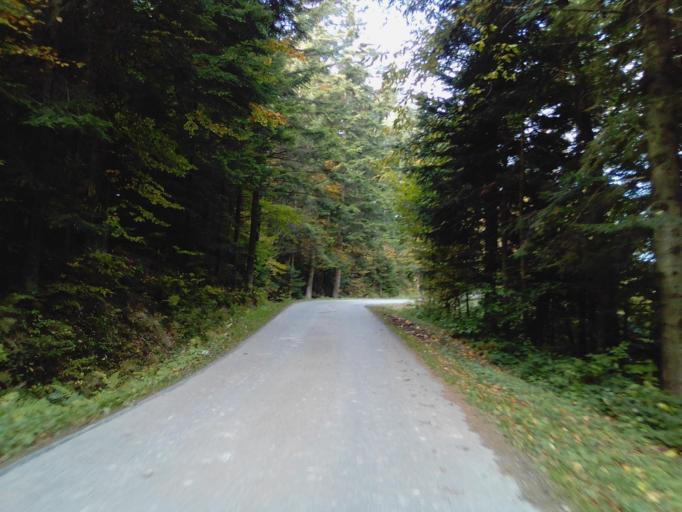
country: PL
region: Subcarpathian Voivodeship
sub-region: Powiat strzyzowski
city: Konieczkowa
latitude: 49.8539
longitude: 21.9593
